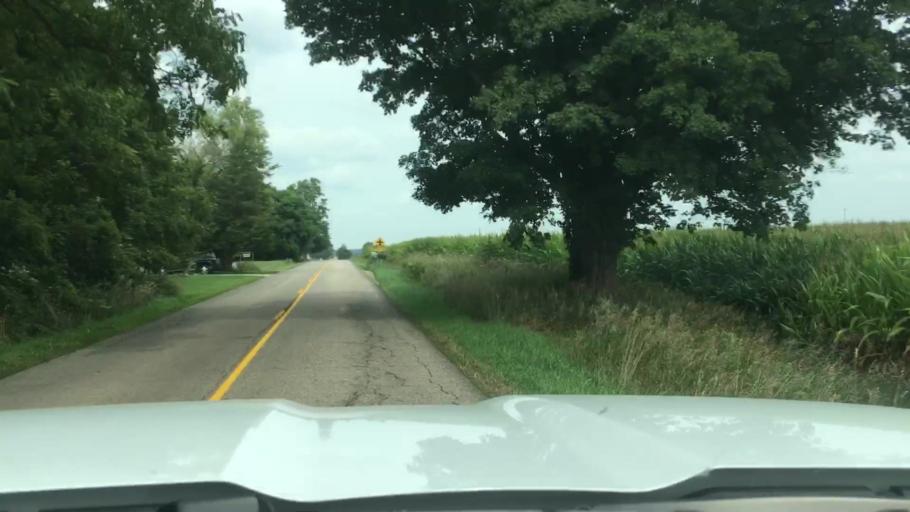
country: US
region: Michigan
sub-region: Ingham County
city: Webberville
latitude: 42.7052
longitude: -84.1913
